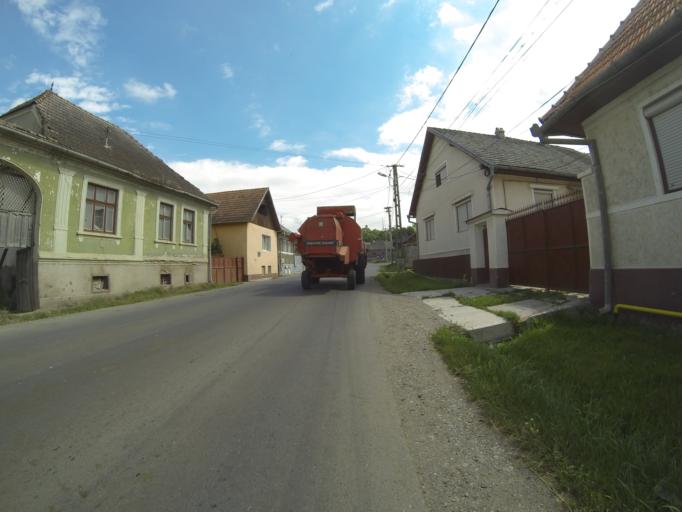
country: RO
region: Brasov
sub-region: Comuna Hoghiz
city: Hoghiz
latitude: 45.9641
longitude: 25.2972
